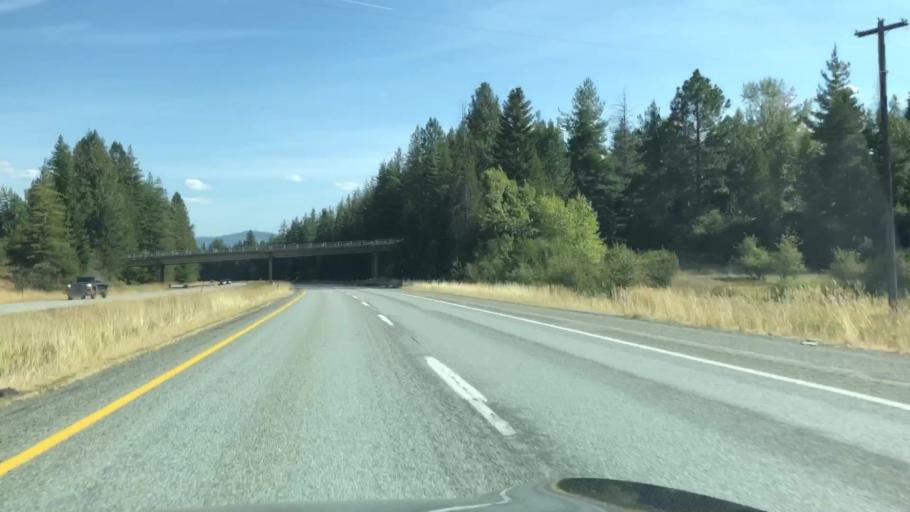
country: US
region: Idaho
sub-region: Shoshone County
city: Pinehurst
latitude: 47.5670
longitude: -116.4099
